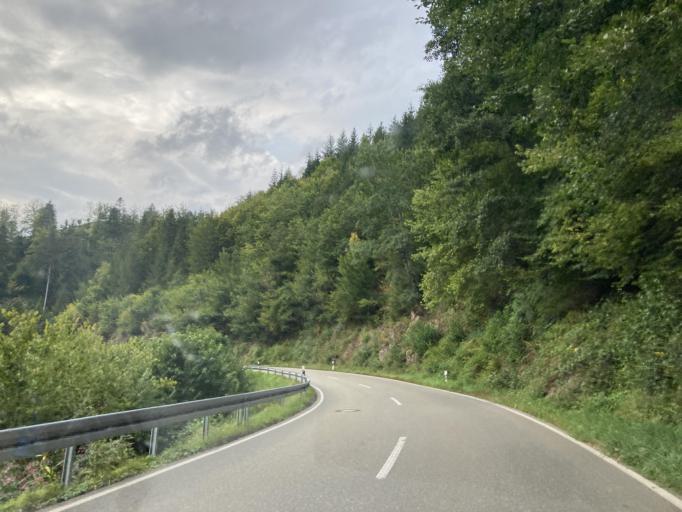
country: DE
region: Baden-Wuerttemberg
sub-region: Freiburg Region
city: Schonenberg
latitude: 47.7803
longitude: 7.8681
